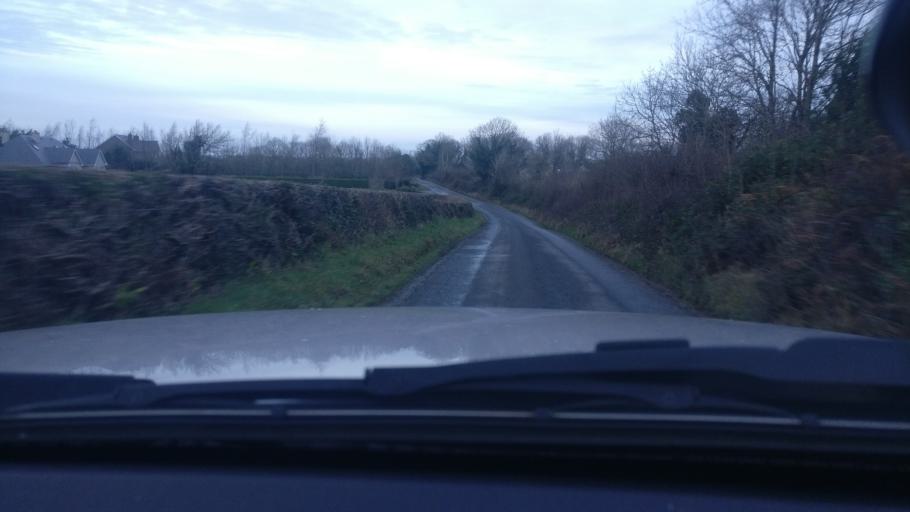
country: IE
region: Connaught
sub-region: County Galway
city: Loughrea
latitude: 53.1908
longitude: -8.5108
